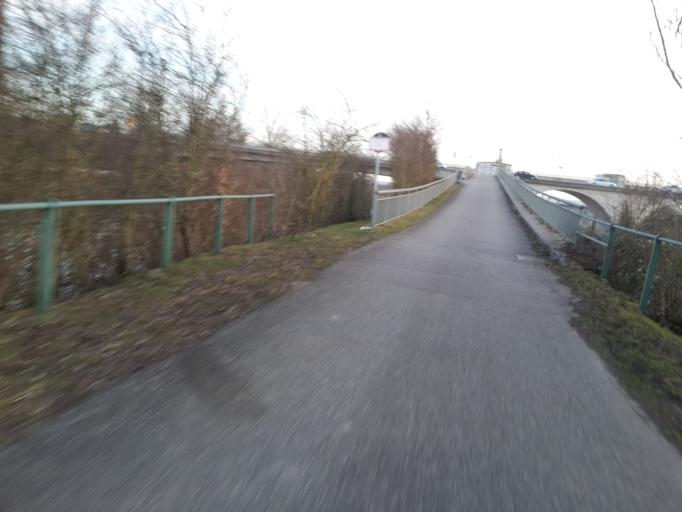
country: DE
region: Baden-Wuerttemberg
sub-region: Regierungsbezirk Stuttgart
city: Neckarsulm
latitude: 49.1903
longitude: 9.2168
